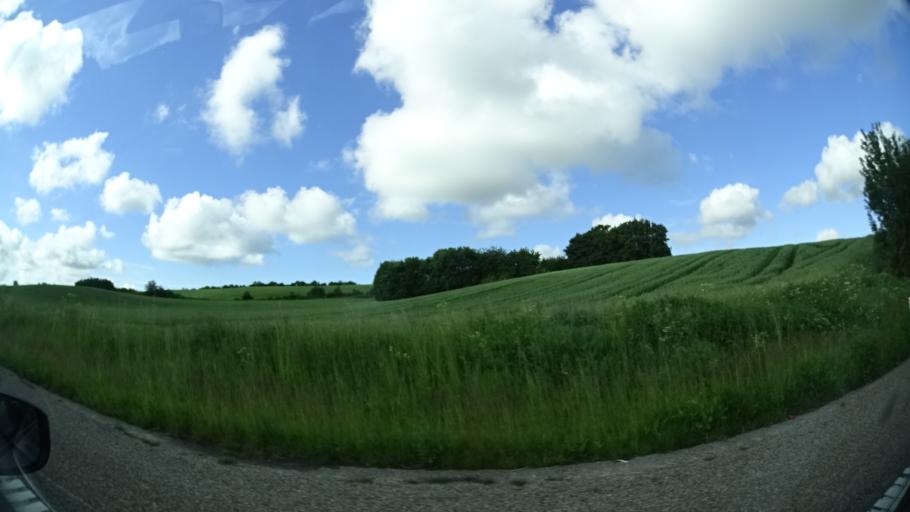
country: DK
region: Central Jutland
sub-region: Syddjurs Kommune
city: Ronde
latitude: 56.3131
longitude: 10.4950
